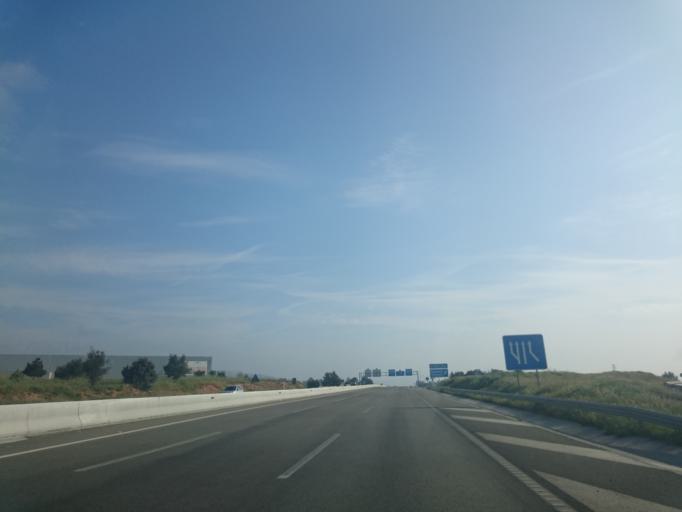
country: ES
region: Catalonia
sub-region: Provincia de Barcelona
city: Sant Fruitos de Bages
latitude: 41.7732
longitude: 1.8754
